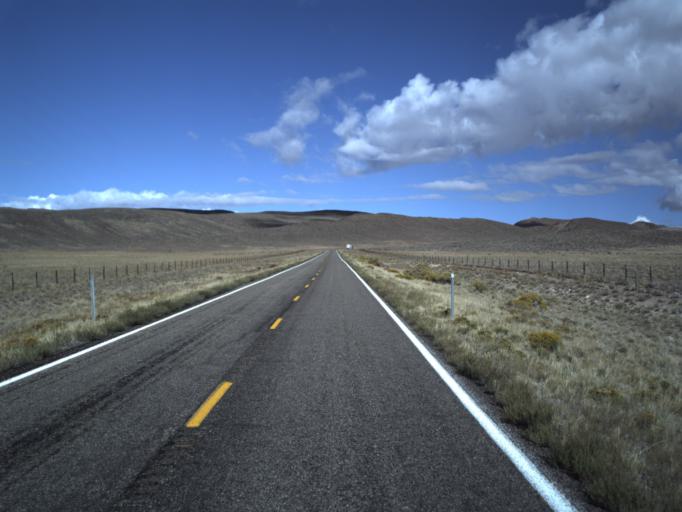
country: US
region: Utah
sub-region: Beaver County
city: Milford
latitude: 38.5973
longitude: -113.8273
